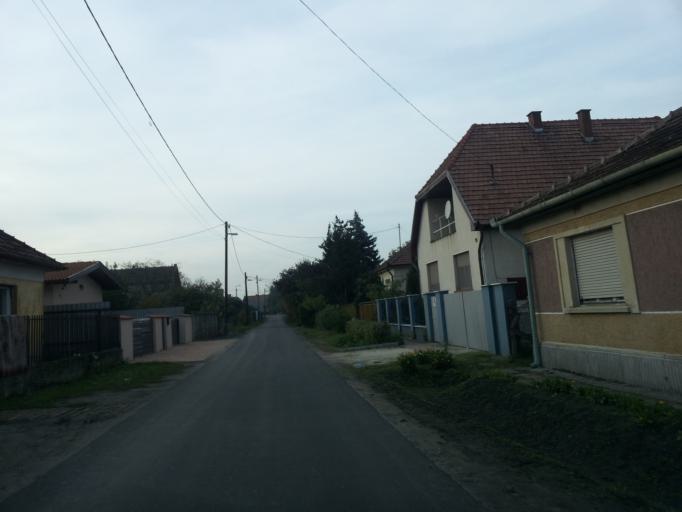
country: HU
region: Pest
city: Nagykata
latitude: 47.4250
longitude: 19.7389
